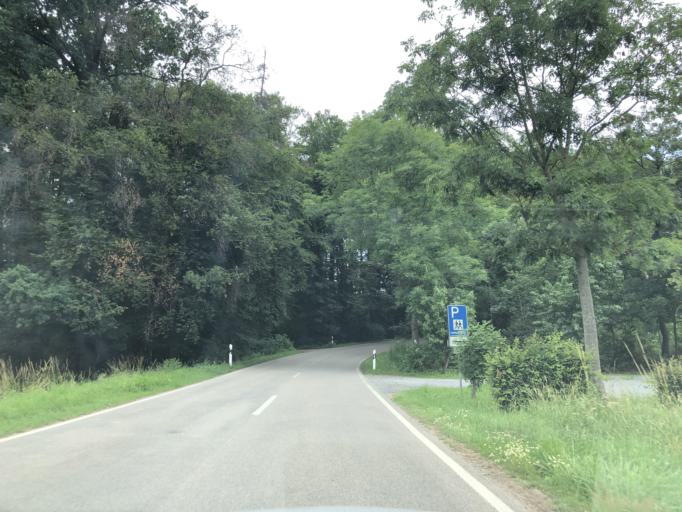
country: DE
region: Hesse
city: Reichelsheim
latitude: 49.7043
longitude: 8.8138
